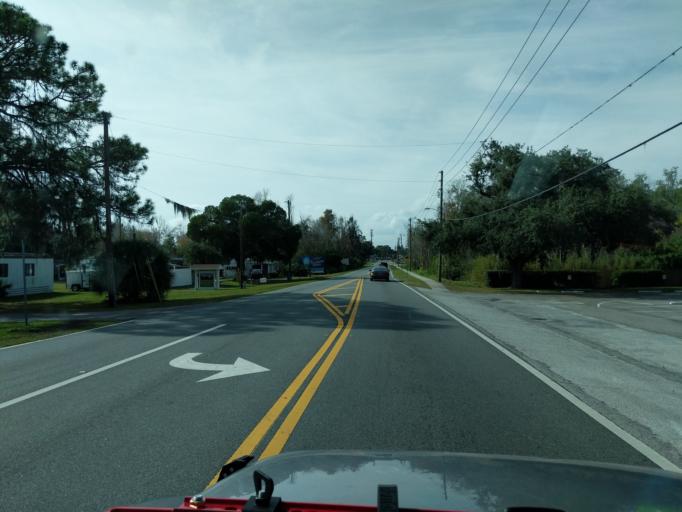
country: US
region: Florida
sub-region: Lake County
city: Tavares
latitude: 28.8041
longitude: -81.7197
